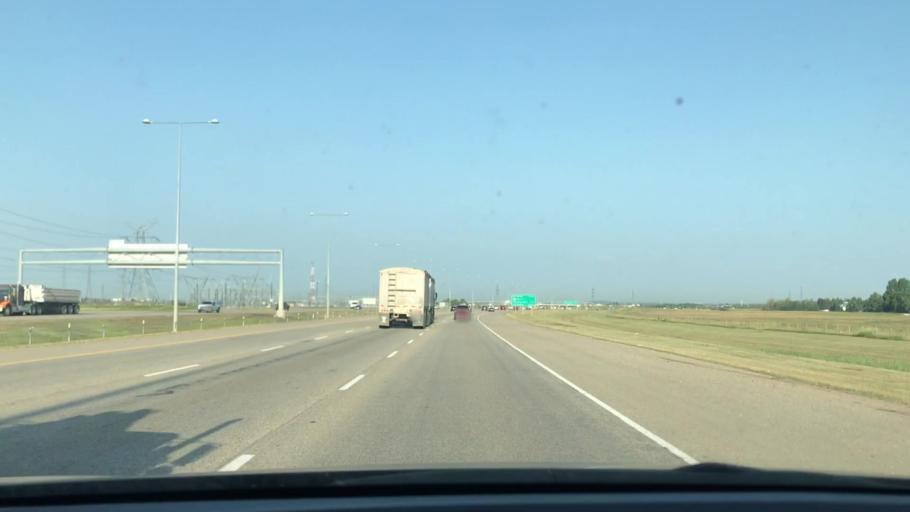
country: CA
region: Alberta
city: Beaumont
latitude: 53.4359
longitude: -113.4417
